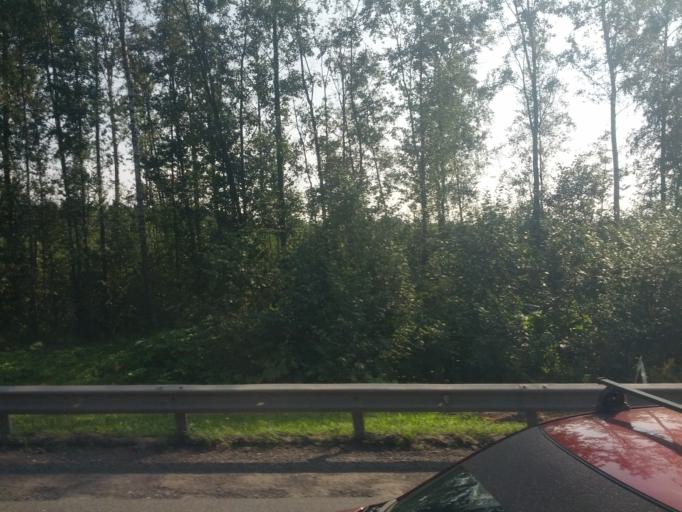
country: RU
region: Leningrad
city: Rybatskoye
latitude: 59.8926
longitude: 30.5405
